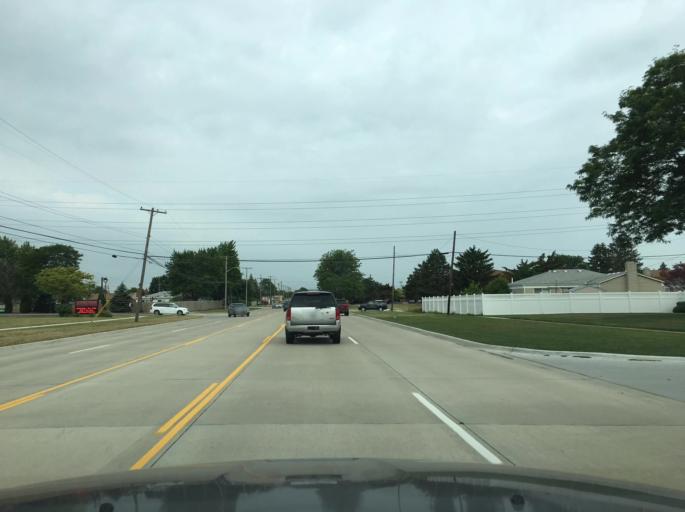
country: US
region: Michigan
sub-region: Macomb County
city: Fraser
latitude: 42.5224
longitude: -82.9822
